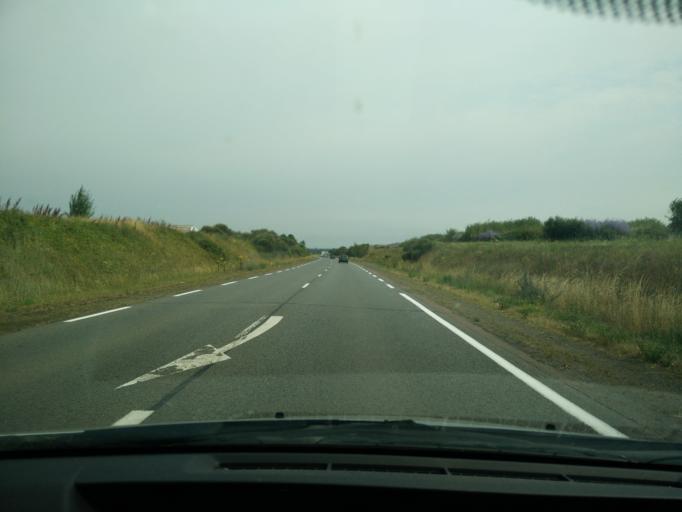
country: FR
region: Poitou-Charentes
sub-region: Departement des Deux-Sevres
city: Sainte-Verge
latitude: 46.9927
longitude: -0.1954
